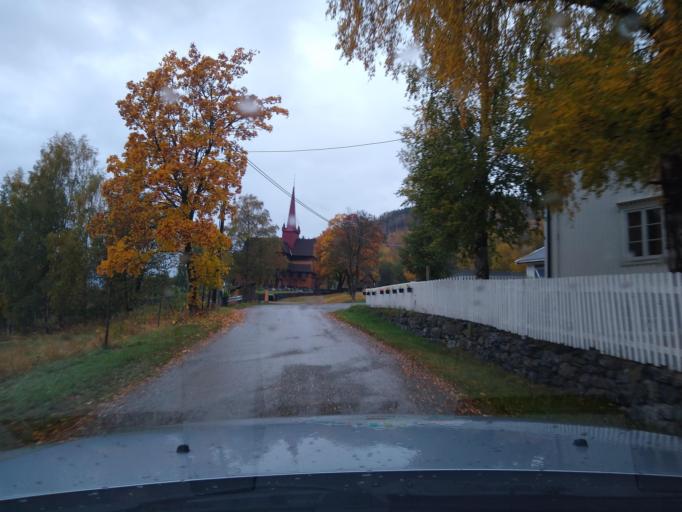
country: NO
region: Oppland
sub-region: Ringebu
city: Ringebu
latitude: 61.5079
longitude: 10.1730
